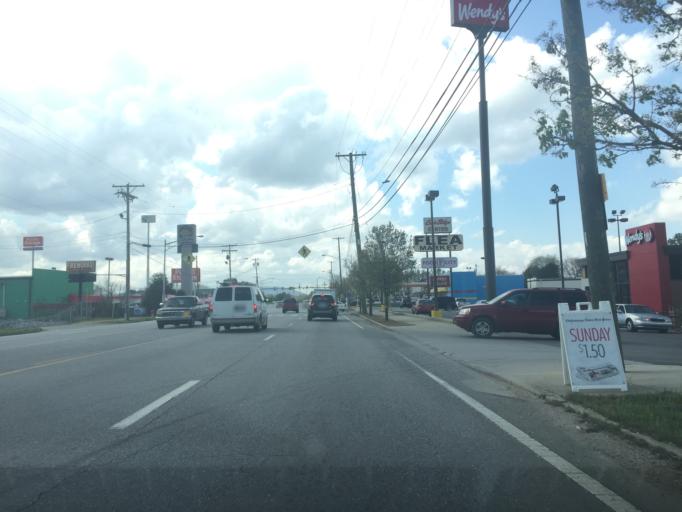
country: US
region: Georgia
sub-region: Catoosa County
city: Indian Springs
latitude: 34.9896
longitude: -85.1968
